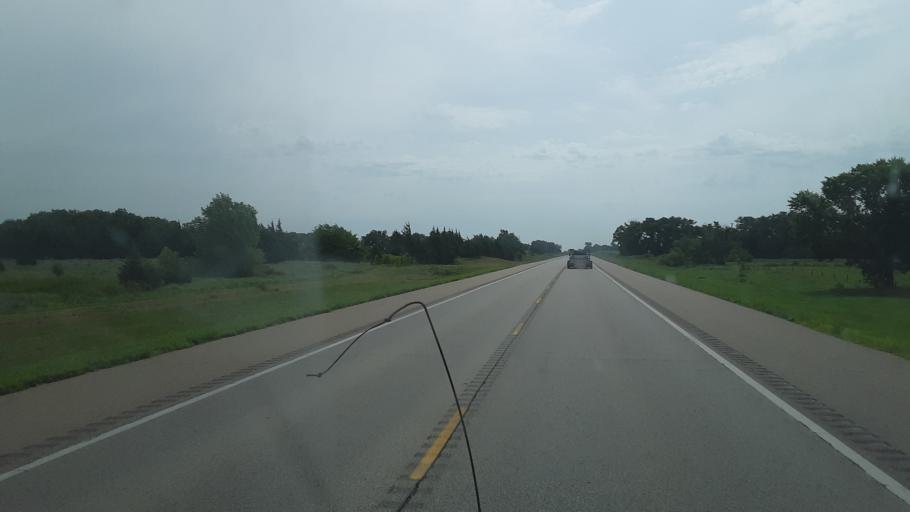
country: US
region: Kansas
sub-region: Rice County
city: Sterling
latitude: 37.9845
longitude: -98.3209
